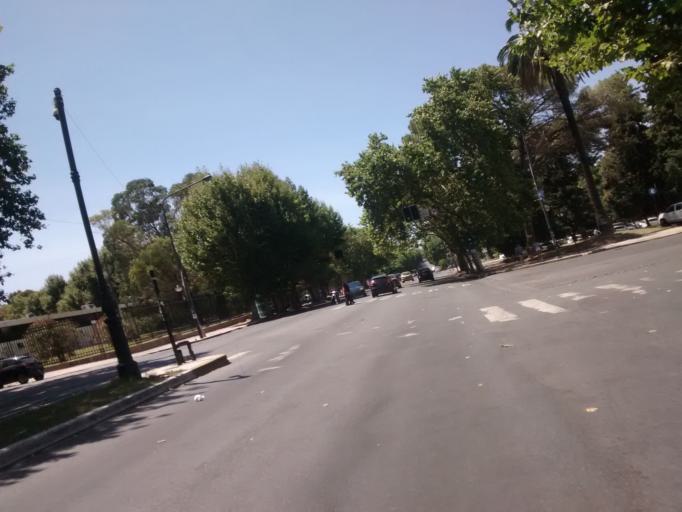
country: AR
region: Buenos Aires
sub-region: Partido de La Plata
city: La Plata
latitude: -34.9091
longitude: -57.9439
